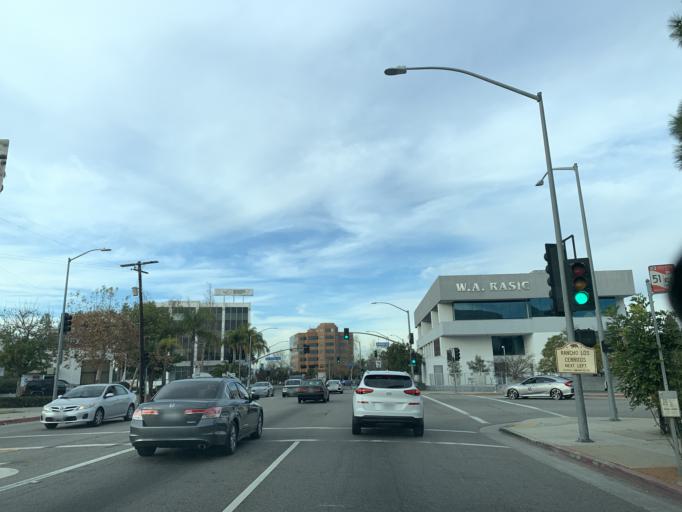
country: US
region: California
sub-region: Los Angeles County
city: Signal Hill
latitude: 33.8335
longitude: -118.1893
